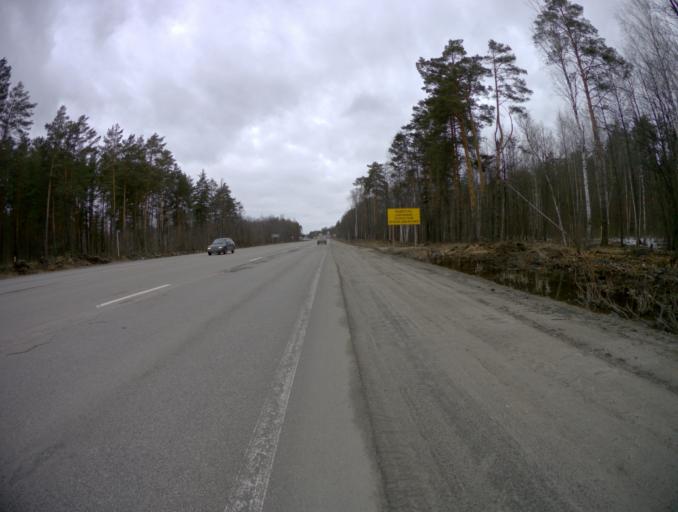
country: RU
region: Vladimir
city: Kommunar
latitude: 56.0925
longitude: 40.4515
